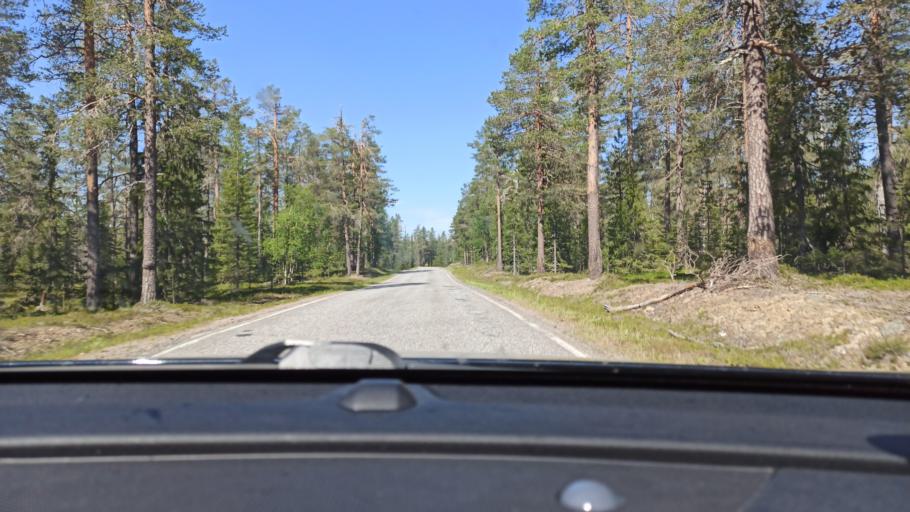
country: FI
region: Lapland
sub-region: Tunturi-Lappi
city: Kolari
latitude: 67.6696
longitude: 24.1555
